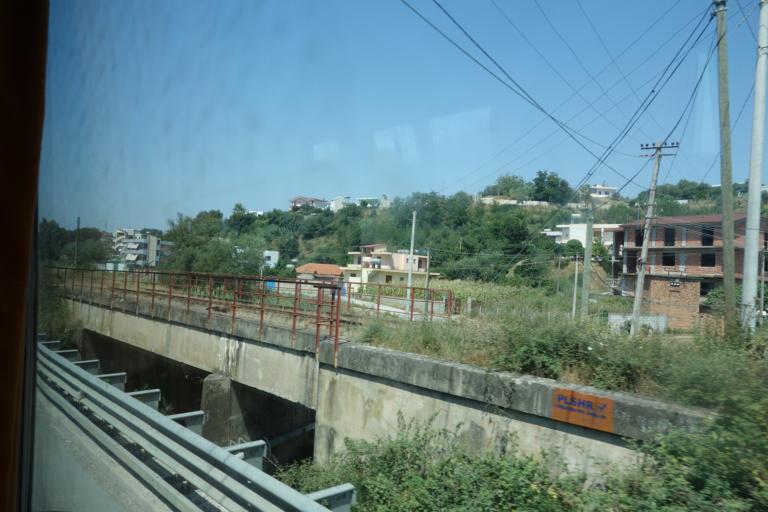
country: AL
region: Durres
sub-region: Rrethi i Durresit
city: Rrashbull
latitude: 41.2873
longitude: 19.5136
